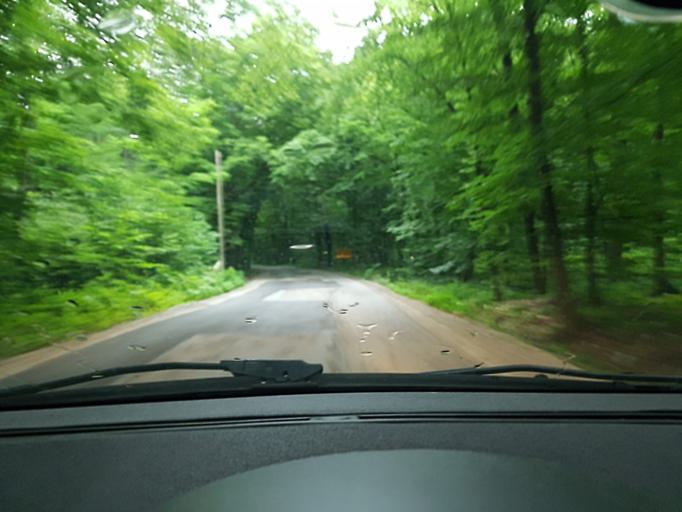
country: HR
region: Zagrebacka
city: Pojatno
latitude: 45.8967
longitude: 15.7916
